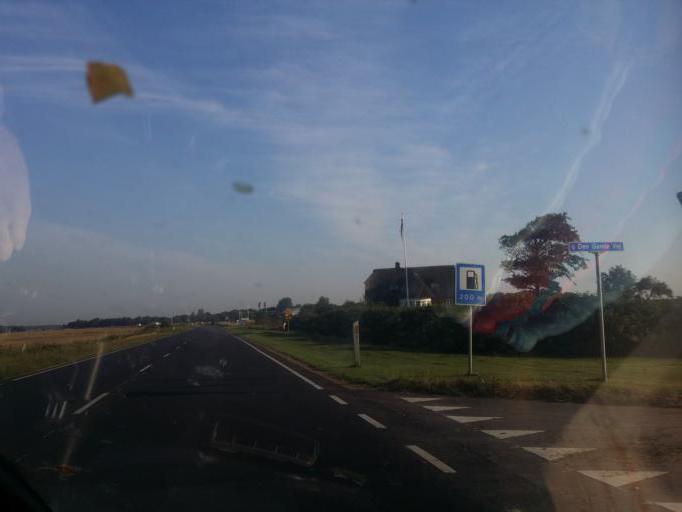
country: DE
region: Schleswig-Holstein
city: Suderlugum
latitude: 54.9066
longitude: 8.9088
